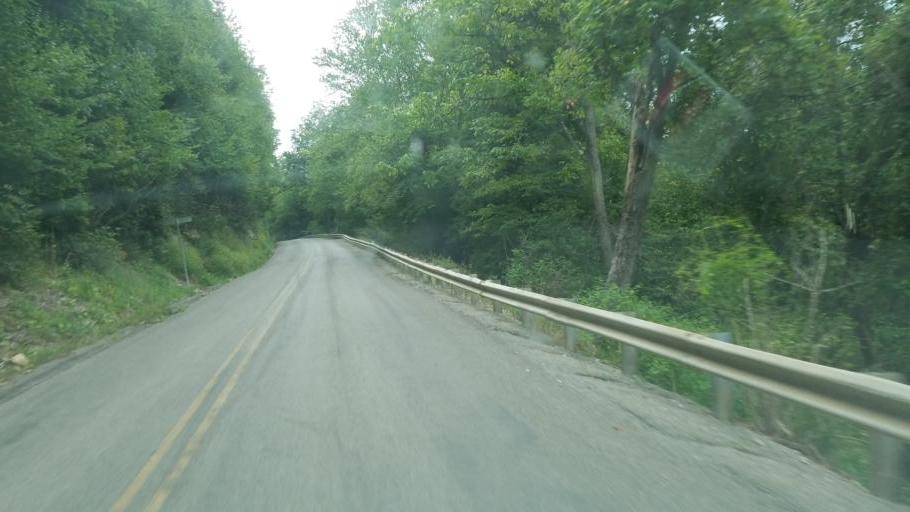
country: US
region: Pennsylvania
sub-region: Clarion County
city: Marianne
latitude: 41.1715
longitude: -79.4721
